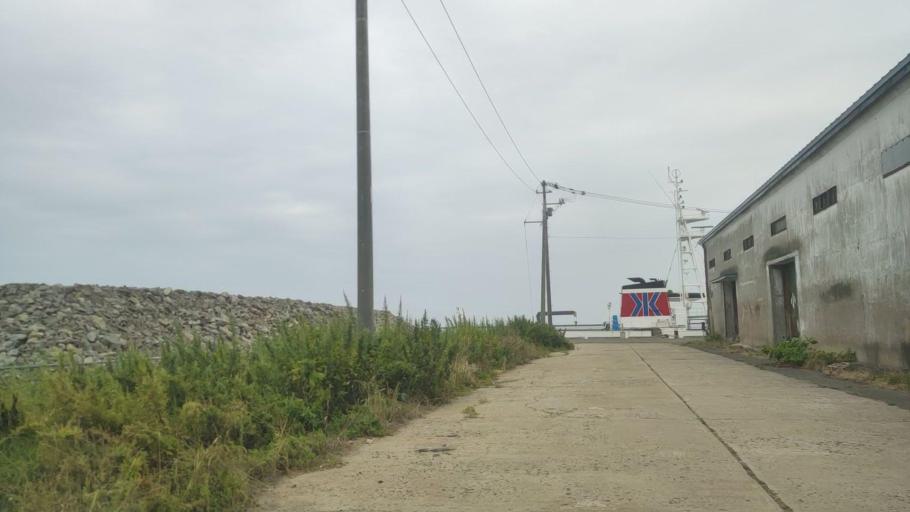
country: JP
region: Hokkaido
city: Otaru
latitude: 43.2004
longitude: 141.0078
